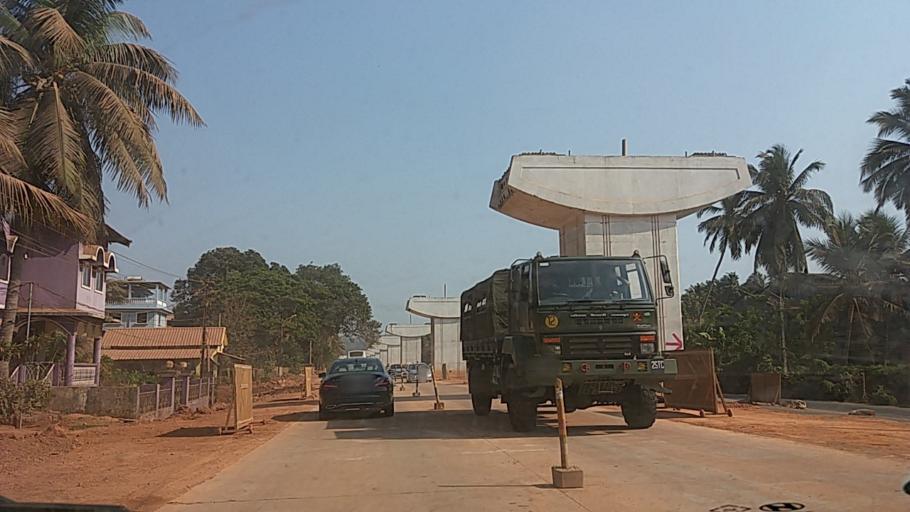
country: IN
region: Goa
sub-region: South Goa
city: Cortalim
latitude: 15.4008
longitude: 73.9087
